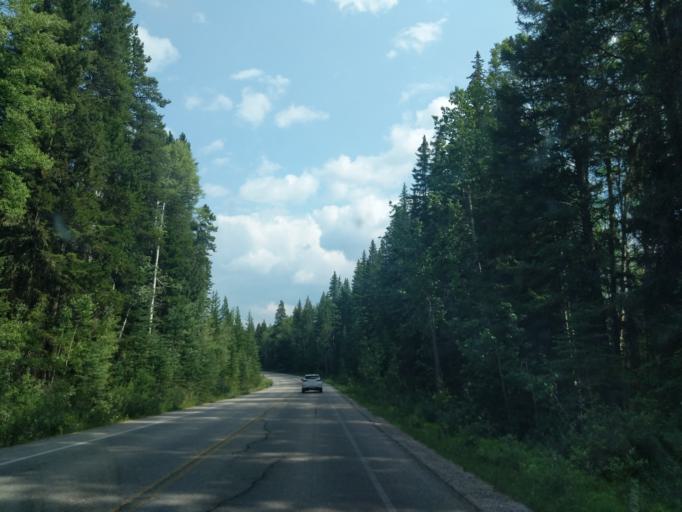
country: CA
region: Alberta
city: Banff
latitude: 51.1729
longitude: -115.7091
